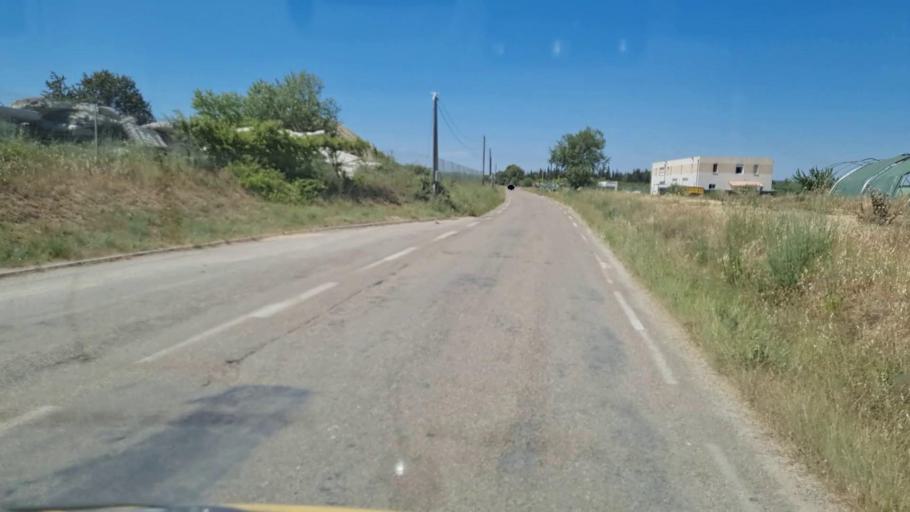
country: FR
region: Languedoc-Roussillon
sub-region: Departement du Gard
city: Codognan
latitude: 43.7183
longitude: 4.2263
